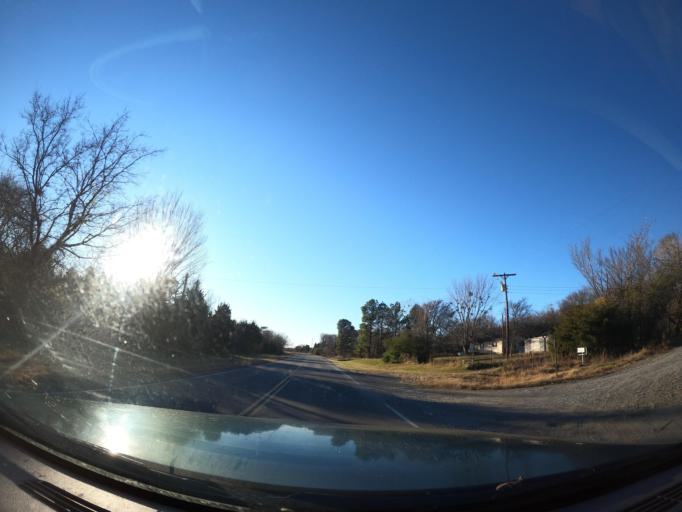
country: US
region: Oklahoma
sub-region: Pittsburg County
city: Hartshorne
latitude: 34.8875
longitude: -95.4791
